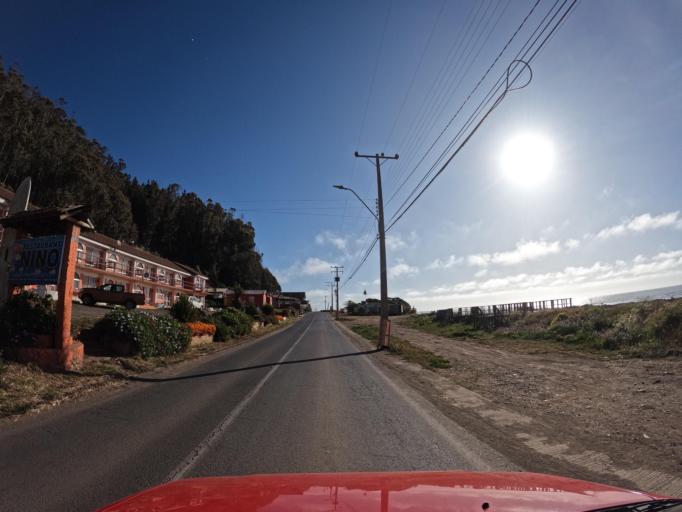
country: CL
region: Maule
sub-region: Provincia de Talca
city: Constitucion
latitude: -34.8893
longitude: -72.1725
